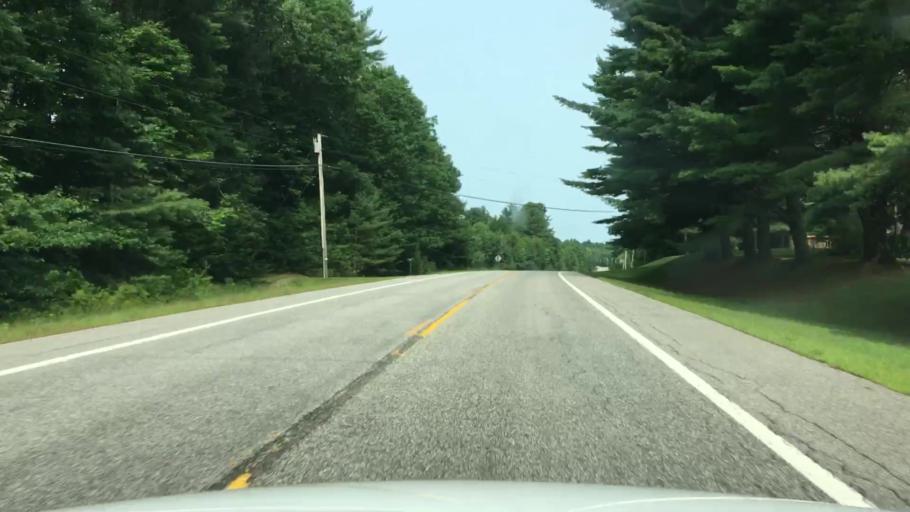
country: US
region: Maine
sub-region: Kennebec County
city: Wayne
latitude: 44.3611
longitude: -70.0855
